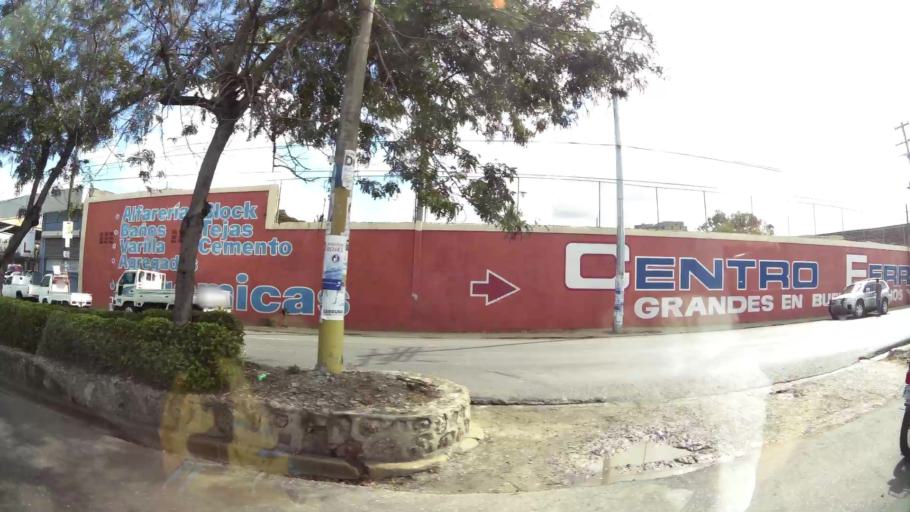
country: DO
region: Santo Domingo
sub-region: Santo Domingo
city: Santo Domingo Este
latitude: 18.5025
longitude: -69.8256
